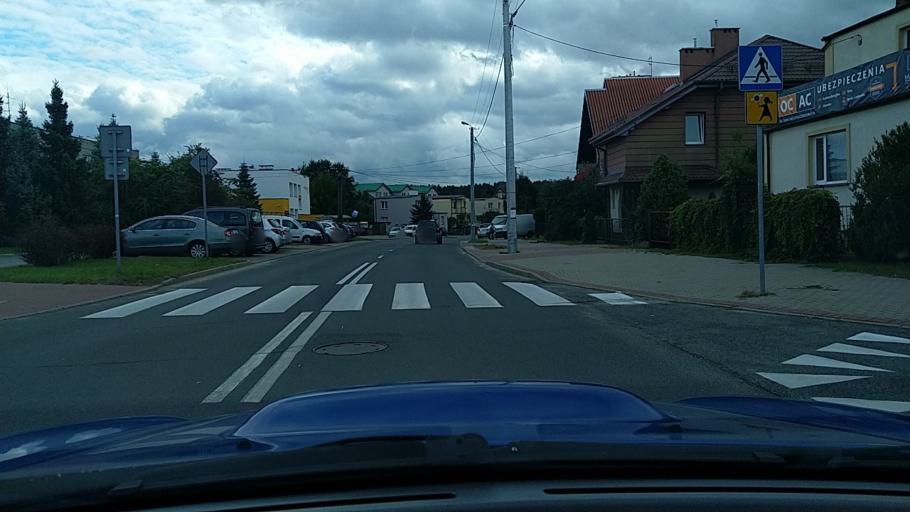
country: PL
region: Warmian-Masurian Voivodeship
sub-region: Olsztyn
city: Kortowo
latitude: 53.7655
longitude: 20.4280
